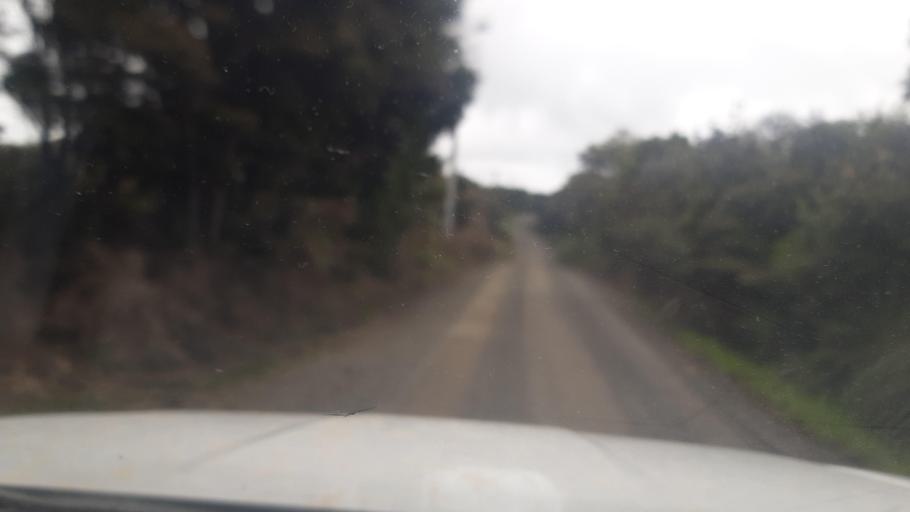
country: NZ
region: Northland
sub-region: Far North District
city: Taipa
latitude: -35.0608
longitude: 173.5326
